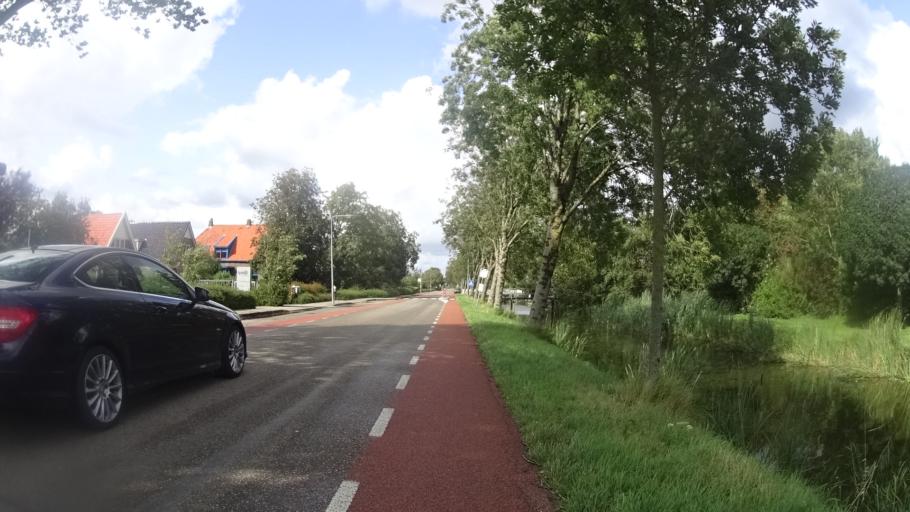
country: NL
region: North Holland
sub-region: Gemeente Schagen
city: Schagen
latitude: 52.8368
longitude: 4.8604
